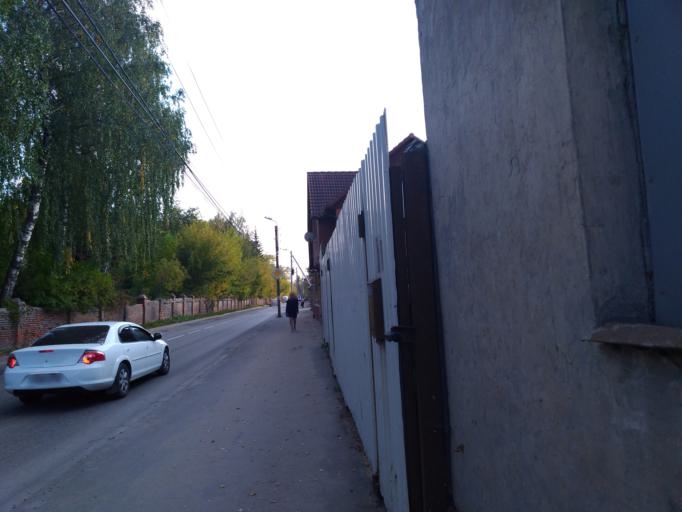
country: RU
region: Kaluga
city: Kaluga
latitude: 54.5254
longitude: 36.2536
